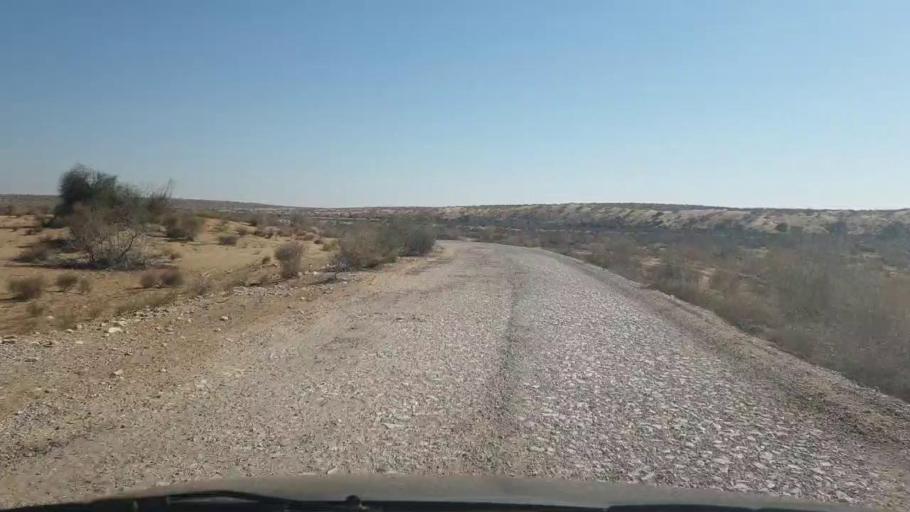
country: PK
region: Sindh
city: Bozdar
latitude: 27.0224
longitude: 68.7164
